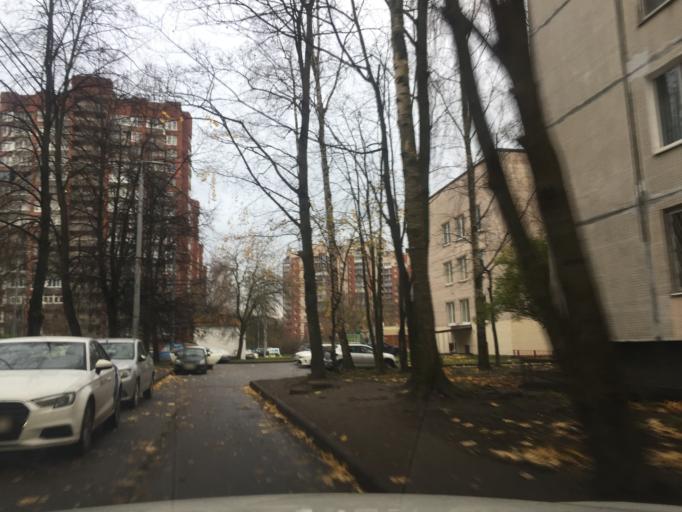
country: RU
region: St.-Petersburg
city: Grazhdanka
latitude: 60.0324
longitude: 30.4223
